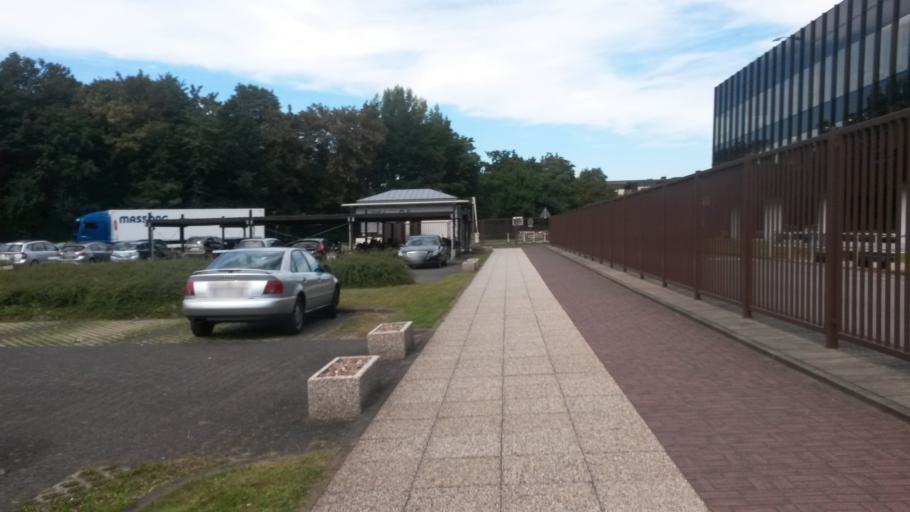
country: DE
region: North Rhine-Westphalia
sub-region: Regierungsbezirk Detmold
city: Paderborn
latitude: 51.7186
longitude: 8.7150
